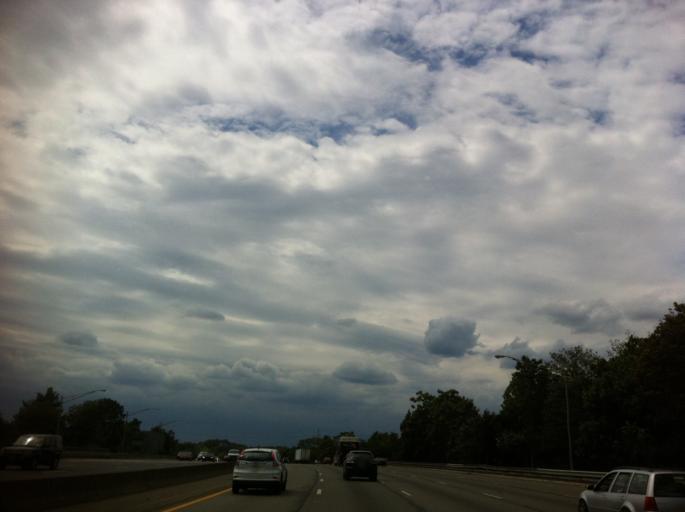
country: US
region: New Jersey
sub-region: Passaic County
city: Woodland Park
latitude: 40.9047
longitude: -74.1922
